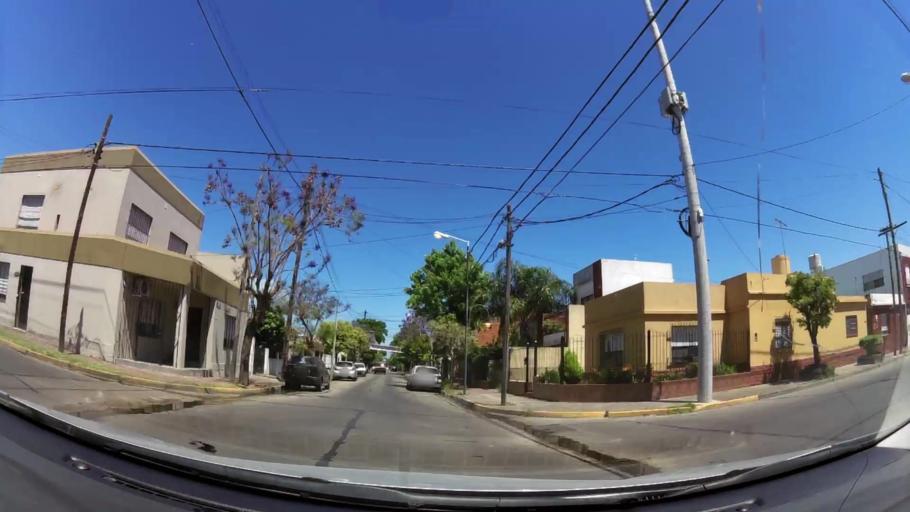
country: AR
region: Buenos Aires
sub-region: Partido de San Isidro
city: San Isidro
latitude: -34.4556
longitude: -58.5470
